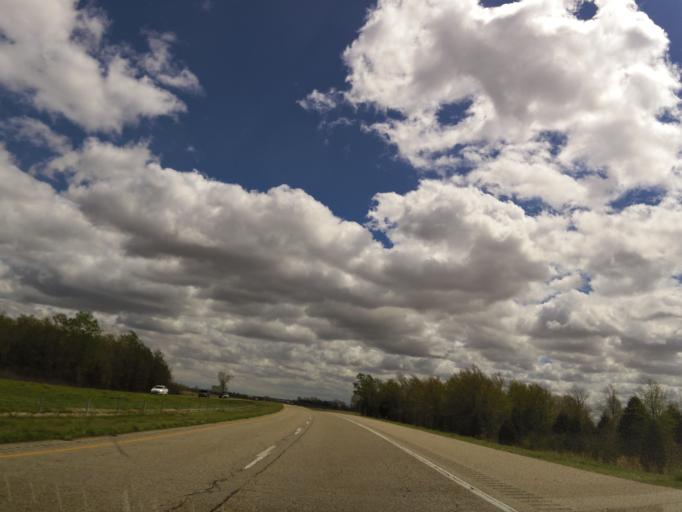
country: US
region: Arkansas
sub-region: Poinsett County
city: Trumann
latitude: 35.6596
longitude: -90.5475
